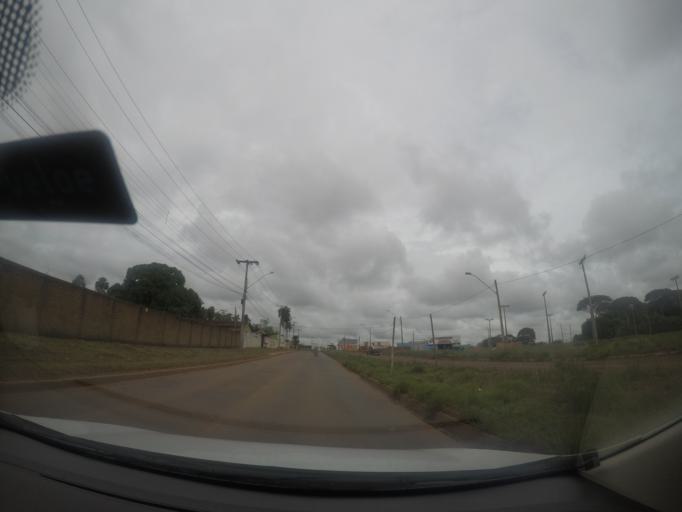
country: BR
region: Goias
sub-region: Goiania
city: Goiania
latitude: -16.6844
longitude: -49.3655
